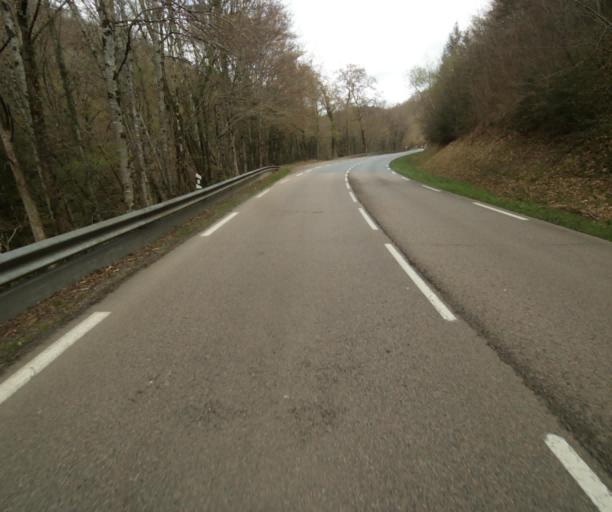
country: FR
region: Limousin
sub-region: Departement de la Correze
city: Sainte-Fortunade
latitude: 45.1880
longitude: 1.8469
